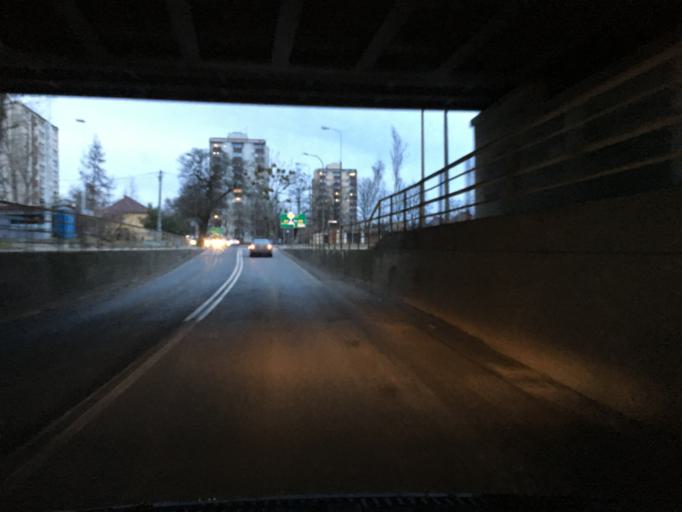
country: PL
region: Opole Voivodeship
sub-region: Powiat opolski
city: Opole
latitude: 50.6606
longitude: 17.8984
